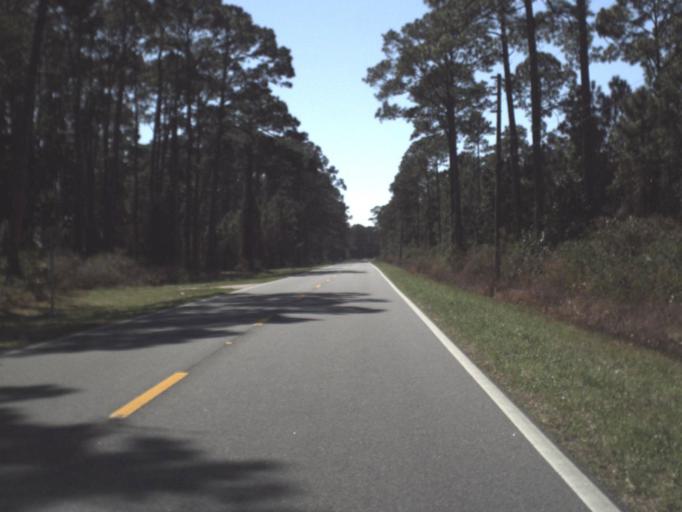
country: US
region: Florida
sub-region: Franklin County
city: Carrabelle
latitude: 29.8926
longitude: -84.5690
